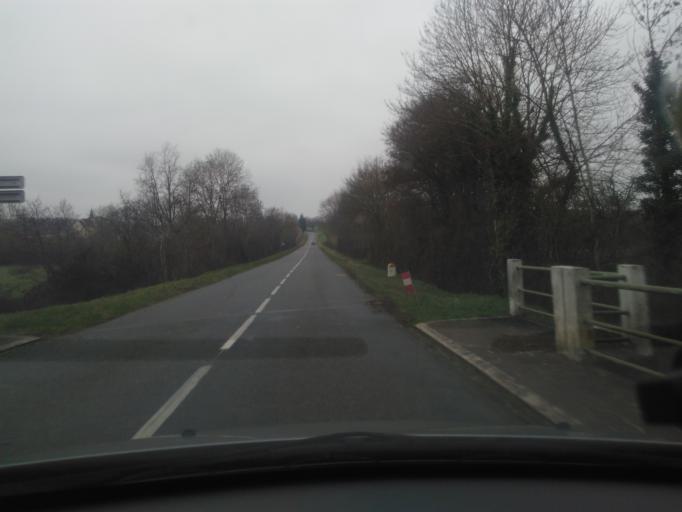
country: FR
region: Centre
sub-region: Departement du Cher
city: Le Chatelet
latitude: 46.6523
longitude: 2.3746
